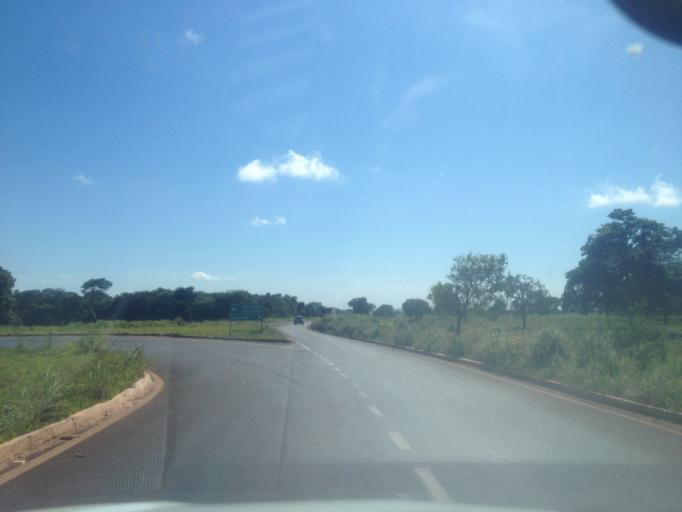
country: BR
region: Minas Gerais
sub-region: Santa Vitoria
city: Santa Vitoria
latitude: -19.0410
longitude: -50.4113
